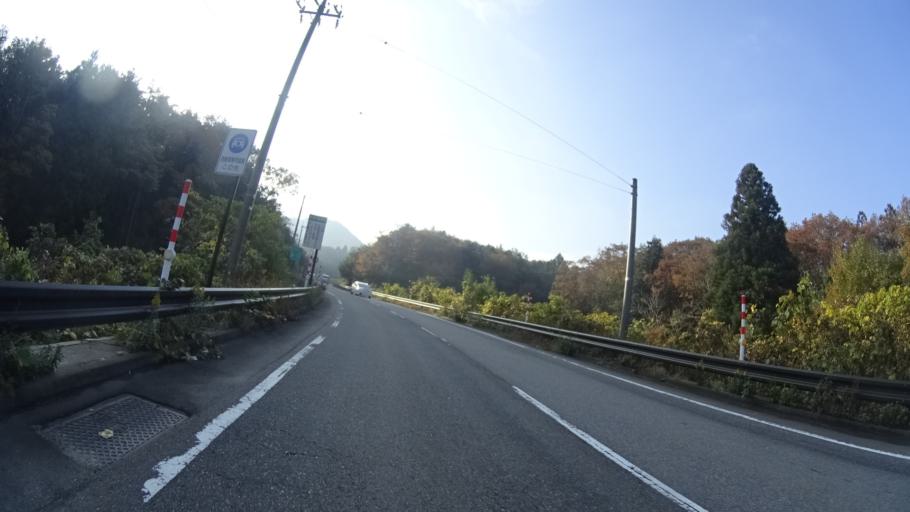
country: JP
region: Ishikawa
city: Nanao
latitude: 37.0241
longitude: 136.9850
